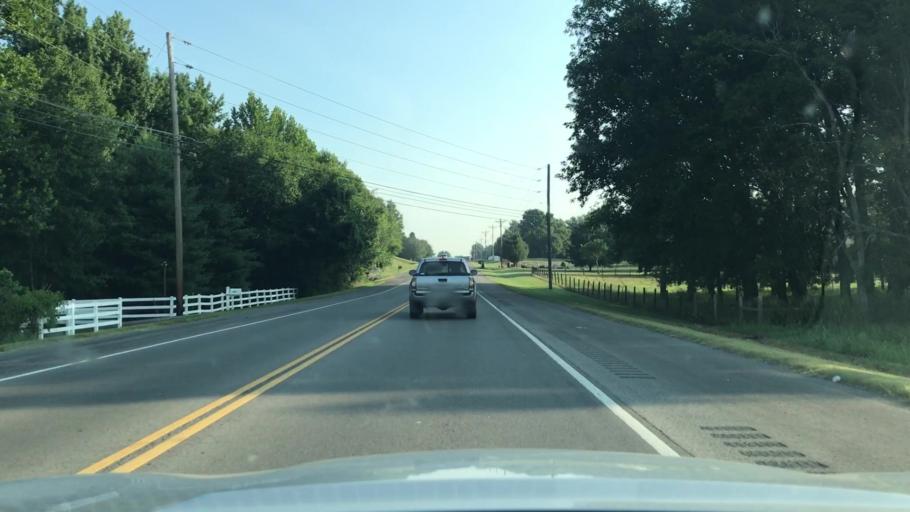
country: US
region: Tennessee
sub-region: Wilson County
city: Rural Hill
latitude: 36.1325
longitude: -86.5194
